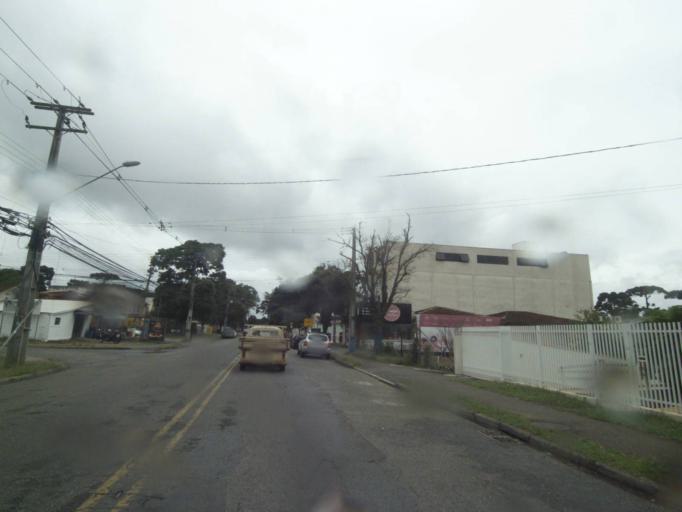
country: BR
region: Parana
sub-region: Curitiba
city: Curitiba
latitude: -25.4453
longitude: -49.3460
